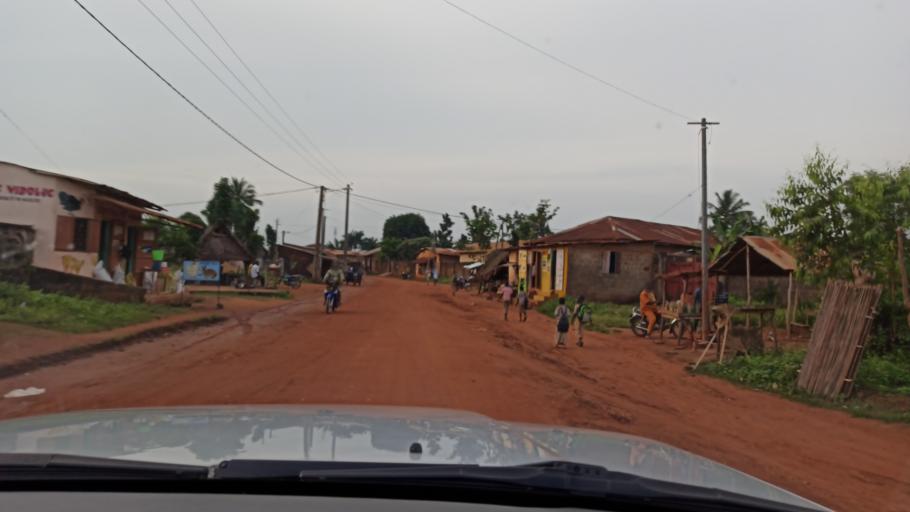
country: BJ
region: Queme
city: Porto-Novo
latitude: 6.5252
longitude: 2.6711
